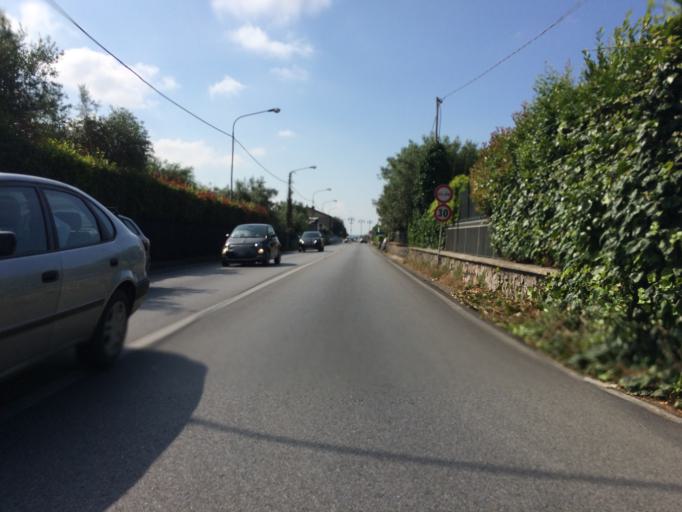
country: IT
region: Tuscany
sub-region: Provincia di Massa-Carrara
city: Capanne-Prato-Cinquale
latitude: 44.0100
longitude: 10.1593
